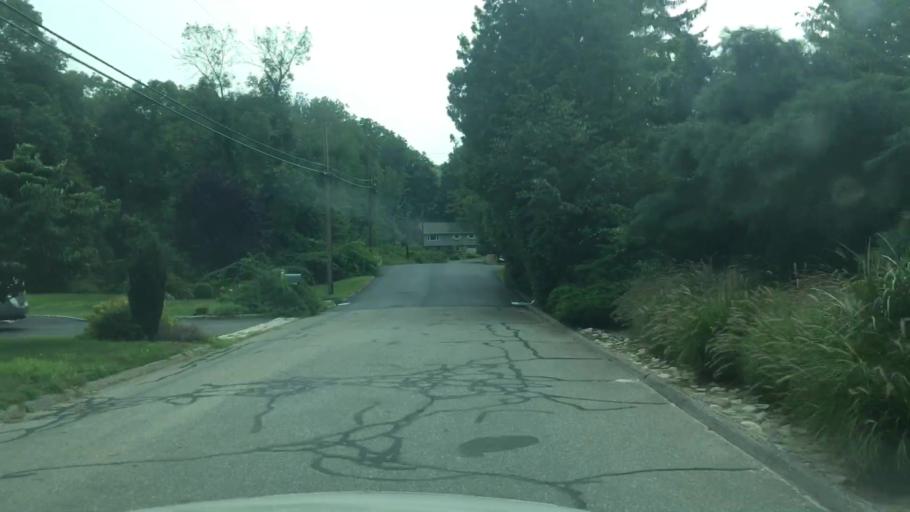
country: US
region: Connecticut
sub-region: Middlesex County
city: Deep River Center
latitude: 41.3496
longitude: -72.4319
